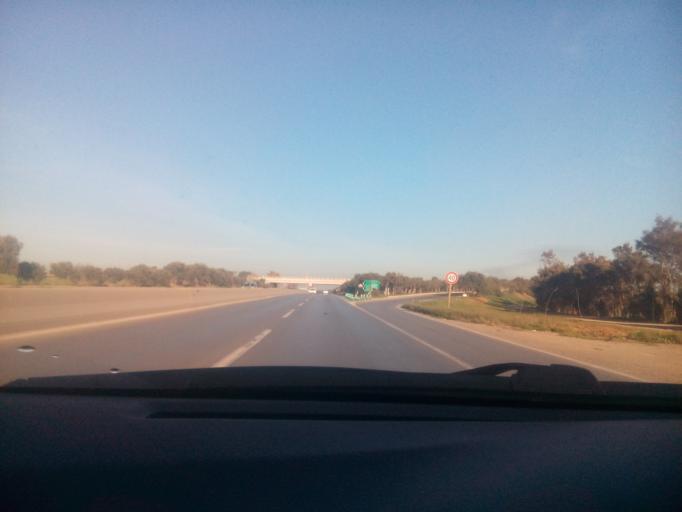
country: DZ
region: Oran
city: Bir el Djir
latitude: 35.7471
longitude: -0.4933
